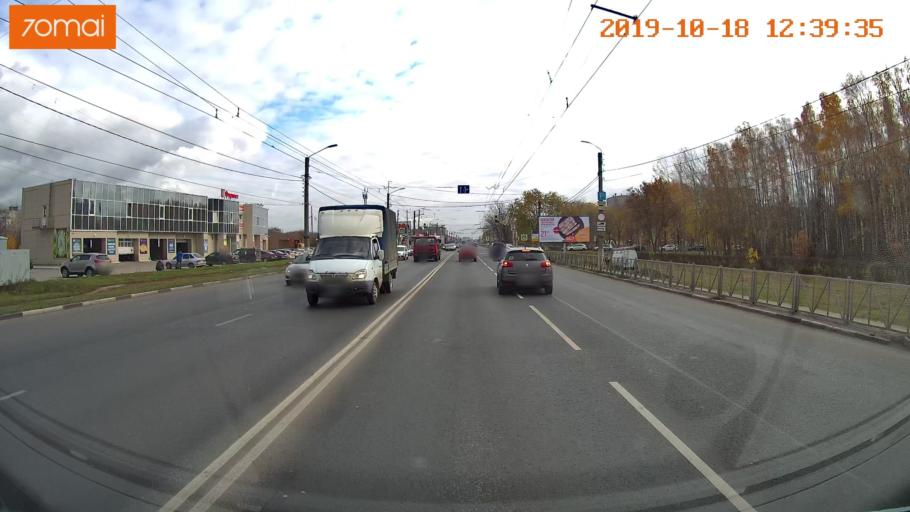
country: RU
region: Rjazan
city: Ryazan'
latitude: 54.6496
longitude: 39.6465
